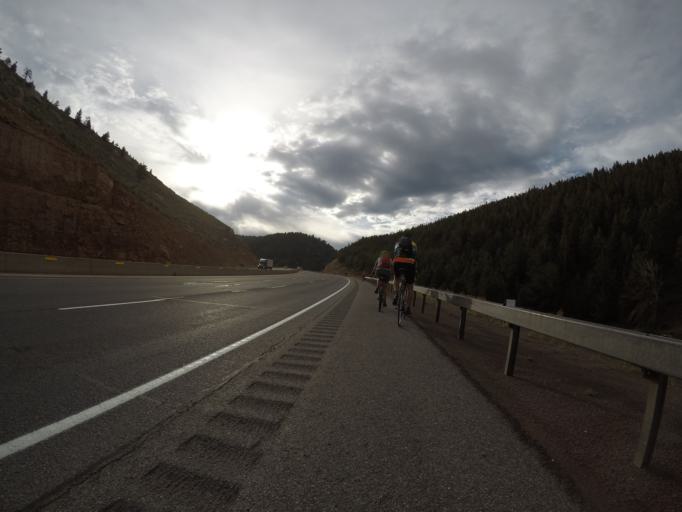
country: US
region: Wyoming
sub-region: Albany County
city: Laramie
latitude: 41.2658
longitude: -105.4741
